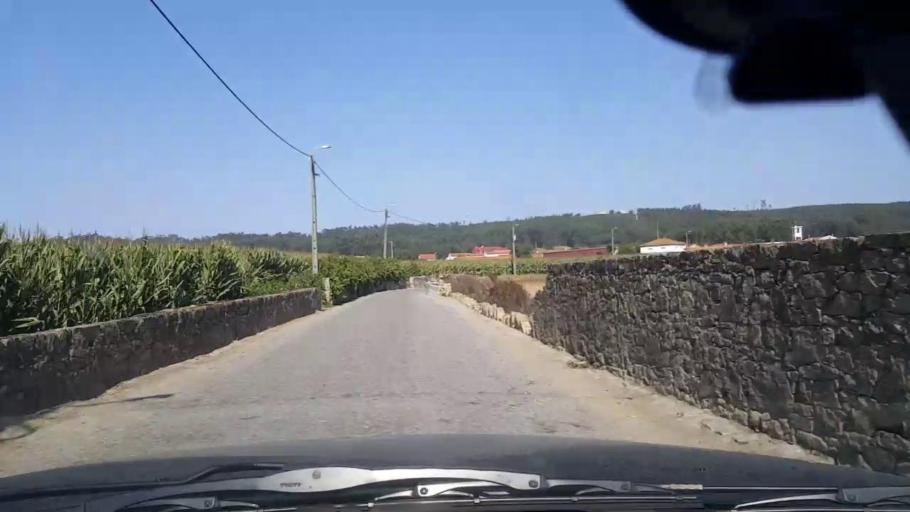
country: PT
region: Porto
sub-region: Povoa de Varzim
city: Pedroso
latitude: 41.4119
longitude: -8.7035
